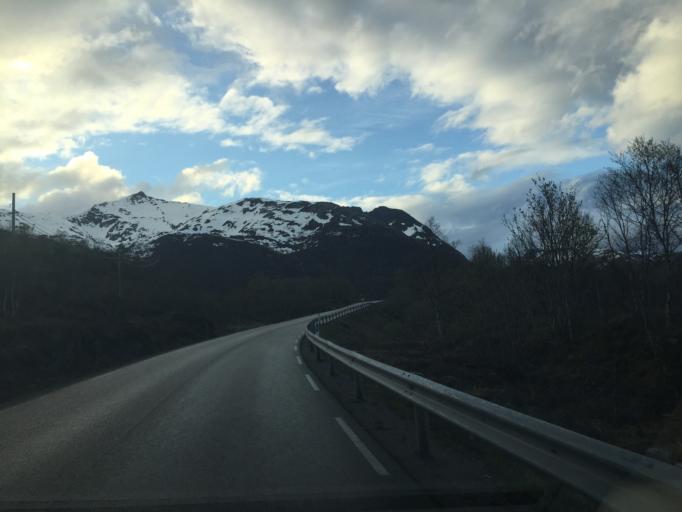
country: NO
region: Nordland
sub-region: Vagan
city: Svolvaer
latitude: 68.3203
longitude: 14.6996
